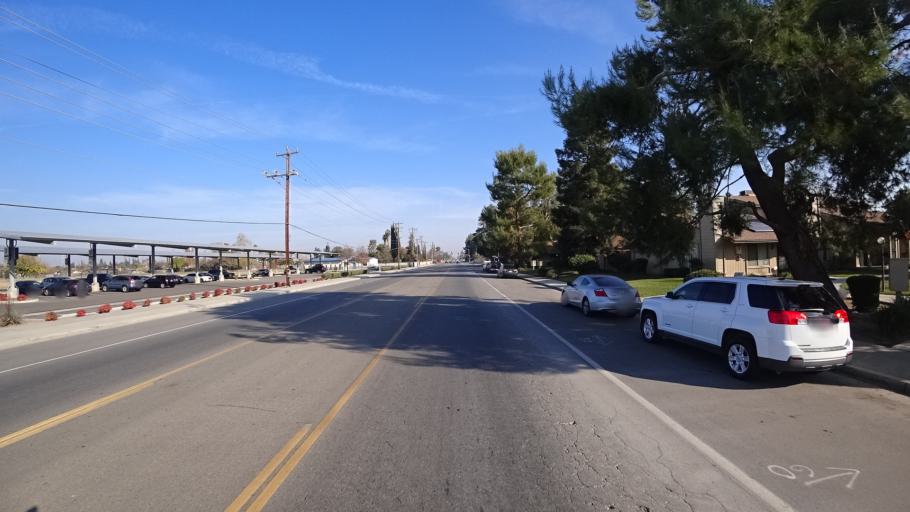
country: US
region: California
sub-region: Kern County
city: Bakersfield
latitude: 35.3250
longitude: -119.0505
